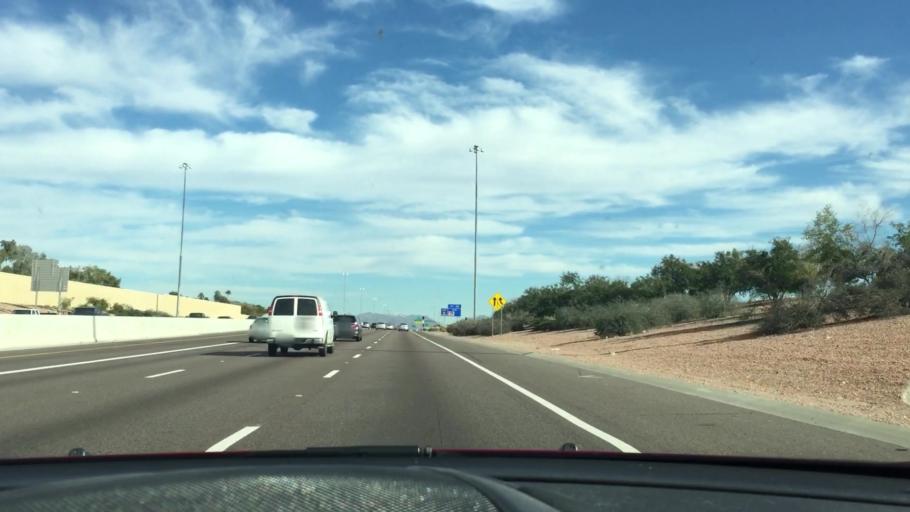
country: US
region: Arizona
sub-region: Maricopa County
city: Glendale
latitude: 33.6723
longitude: -112.0762
